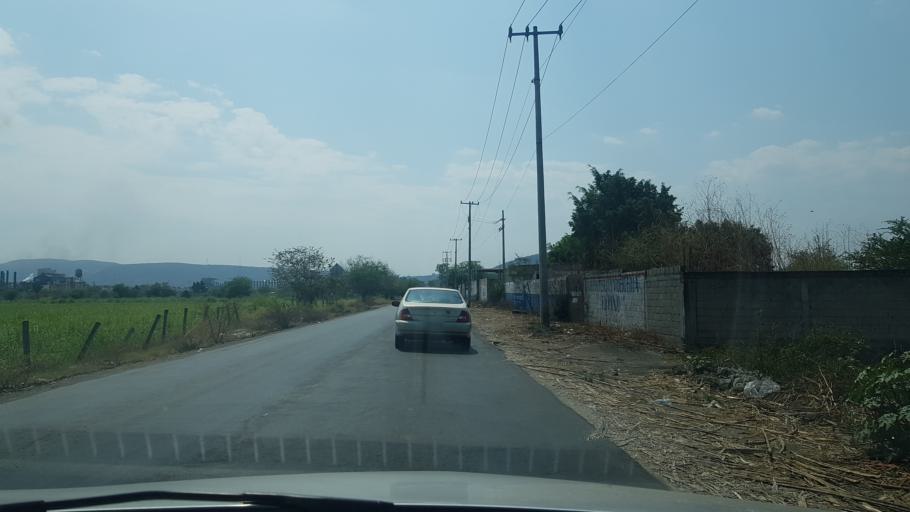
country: MX
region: Morelos
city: Zacatepec
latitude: 18.6589
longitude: -99.1796
